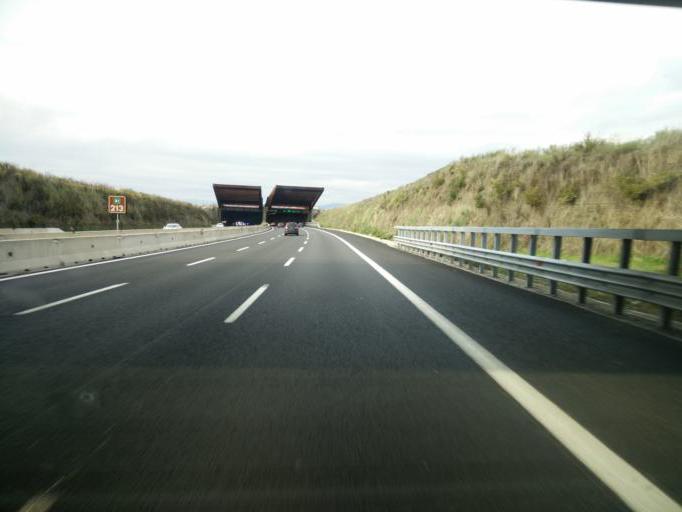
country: IT
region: Tuscany
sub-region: Province of Florence
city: Scandicci
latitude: 43.7607
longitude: 11.1700
